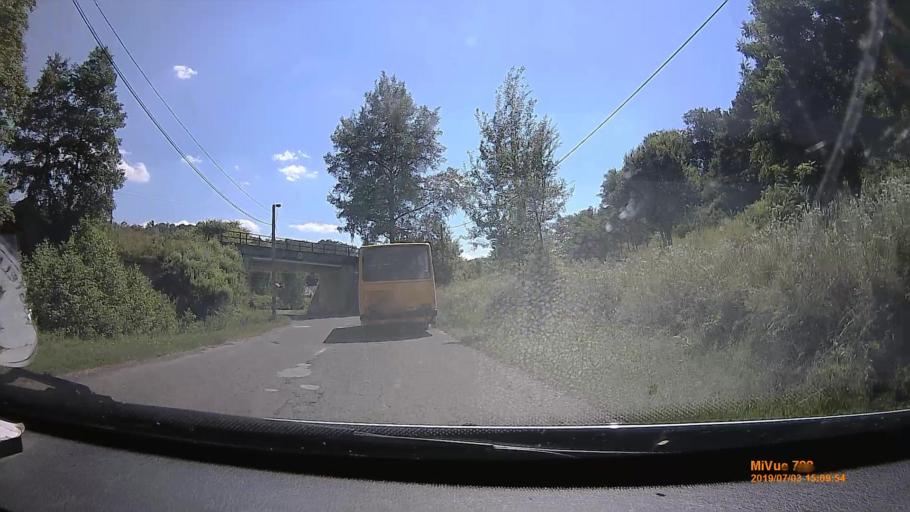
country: HU
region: Borsod-Abauj-Zemplen
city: Ozd
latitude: 48.2343
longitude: 20.3713
